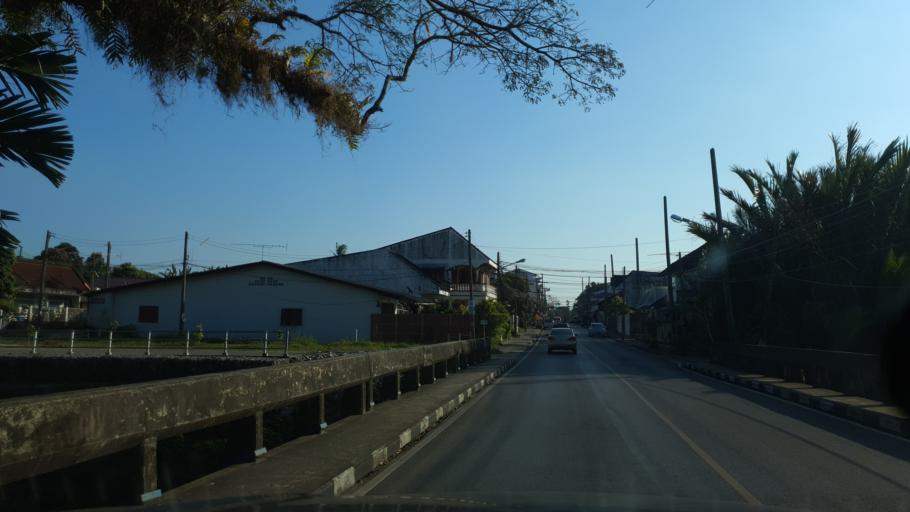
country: TH
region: Krabi
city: Krabi
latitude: 8.1037
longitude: 98.9115
